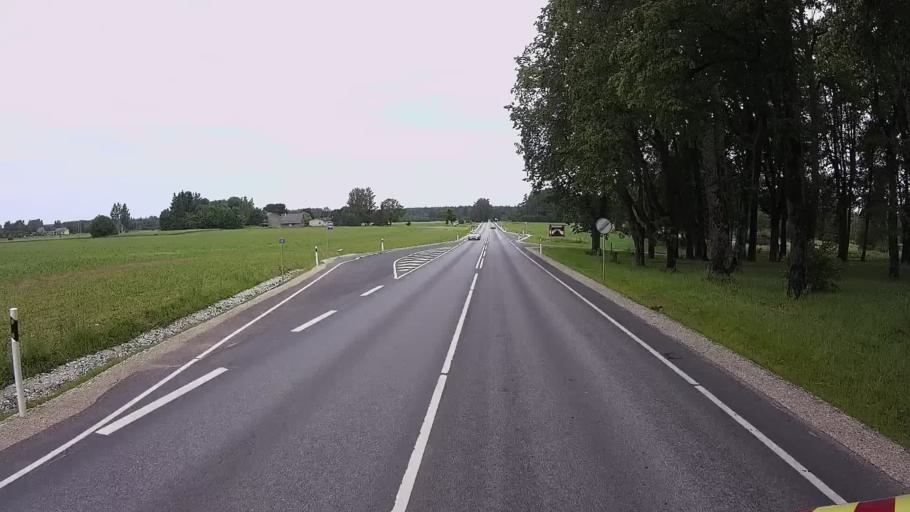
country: EE
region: Viljandimaa
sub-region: Viljandi linn
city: Viljandi
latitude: 58.2732
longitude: 25.5831
